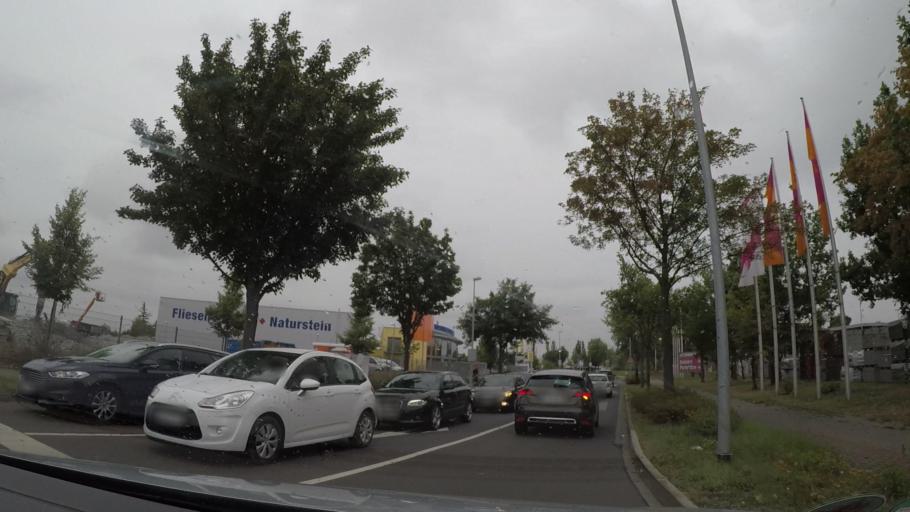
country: DE
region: Saxony-Anhalt
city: Neue Neustadt
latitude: 52.1667
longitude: 11.6084
